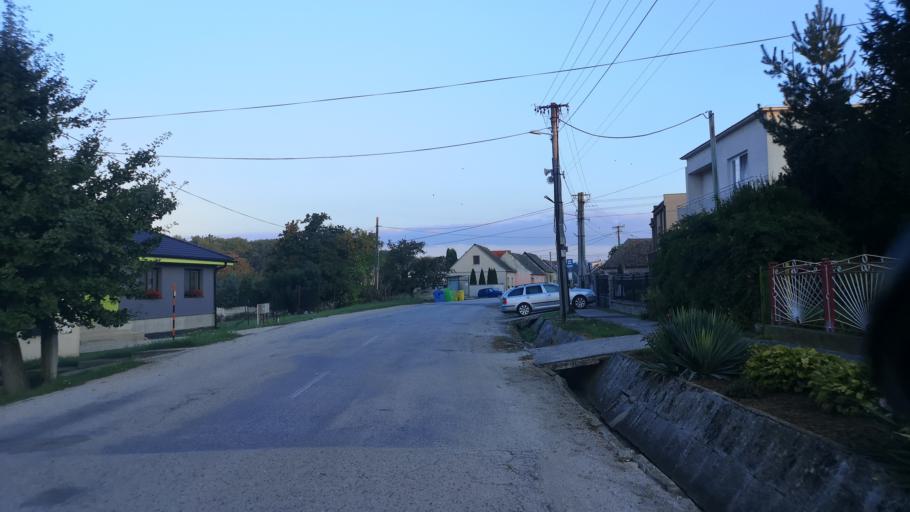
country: SK
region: Trnavsky
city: Smolenice
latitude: 48.5164
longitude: 17.5674
